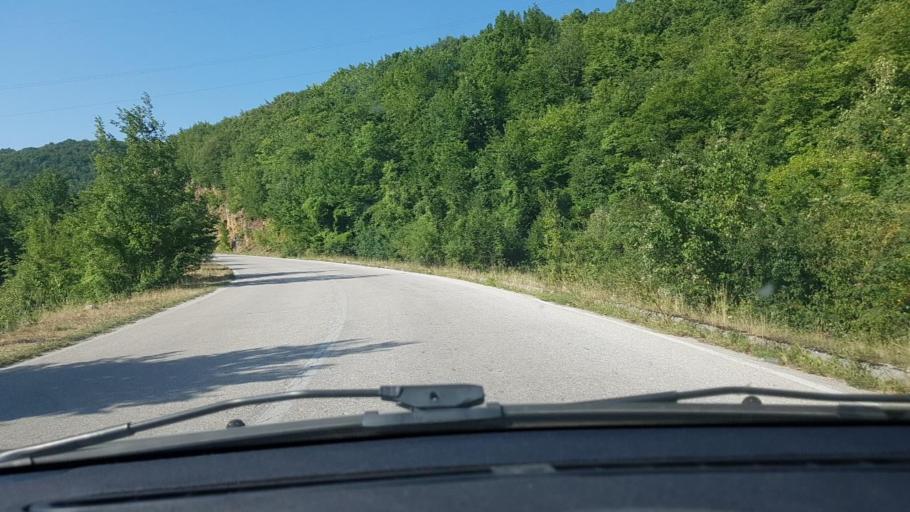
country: BA
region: Federation of Bosnia and Herzegovina
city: Rumboci
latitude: 43.8190
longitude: 17.4456
